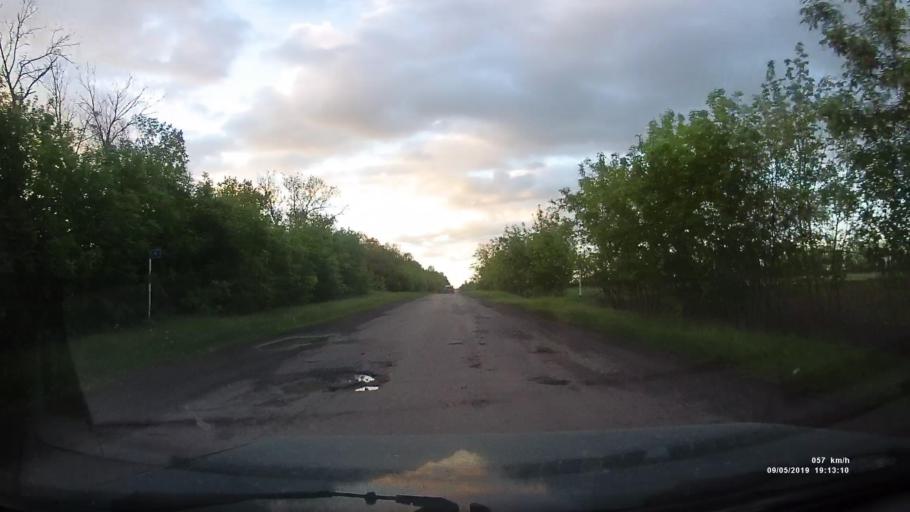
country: RU
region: Krasnodarskiy
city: Kanelovskaya
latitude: 46.7483
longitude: 39.2137
